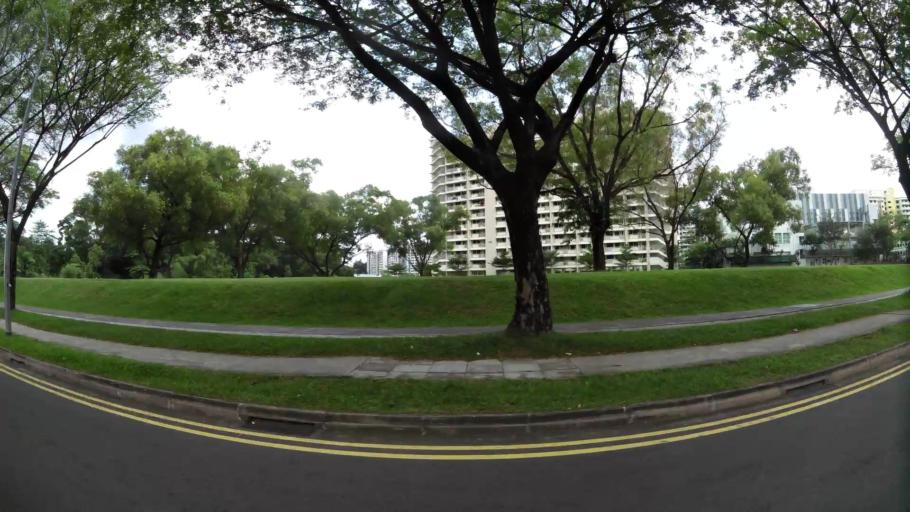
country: MY
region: Johor
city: Kampung Pasir Gudang Baru
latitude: 1.4550
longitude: 103.8193
